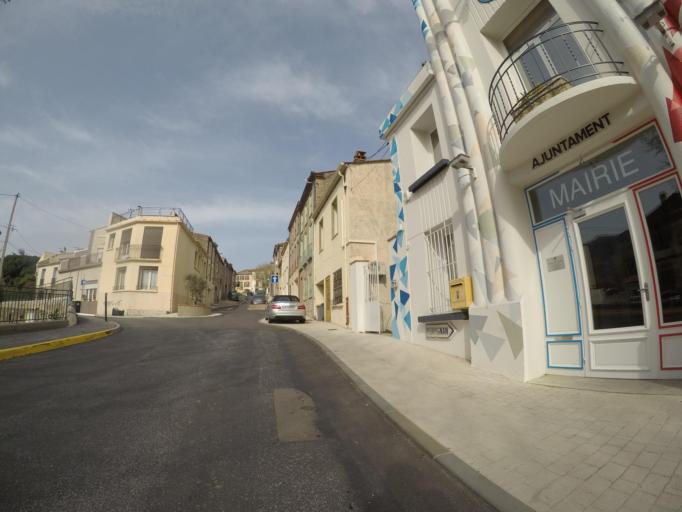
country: FR
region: Languedoc-Roussillon
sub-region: Departement des Pyrenees-Orientales
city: Baixas
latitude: 42.7789
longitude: 2.7874
